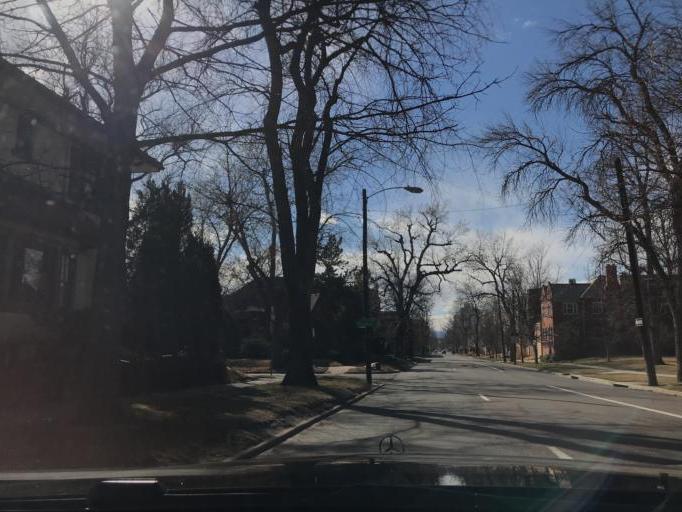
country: US
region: Colorado
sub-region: Denver County
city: Denver
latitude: 39.7291
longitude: -104.9678
